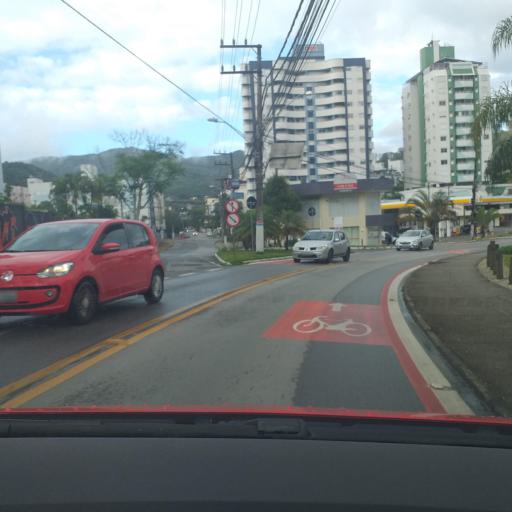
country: BR
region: Santa Catarina
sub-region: Florianopolis
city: Corrego Grande
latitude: -27.6003
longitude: -48.4991
